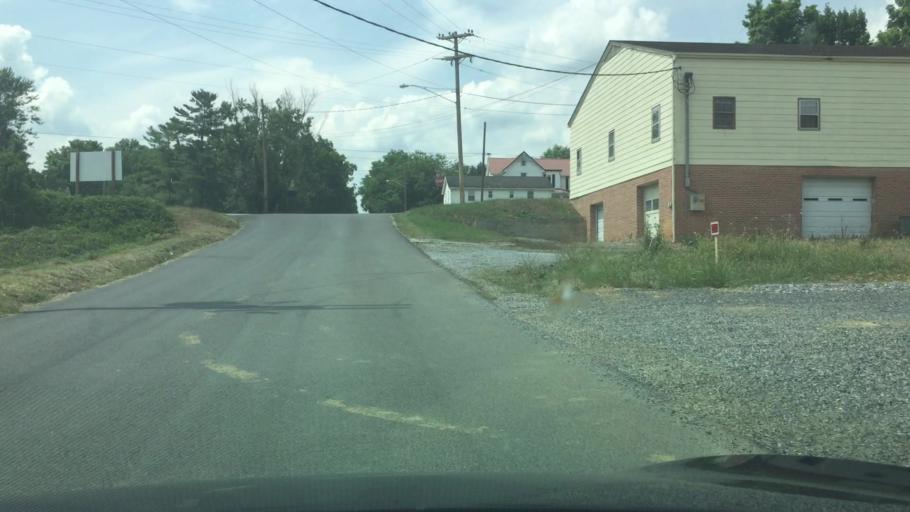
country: US
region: Virginia
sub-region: Wythe County
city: Wytheville
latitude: 36.9430
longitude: -81.0803
